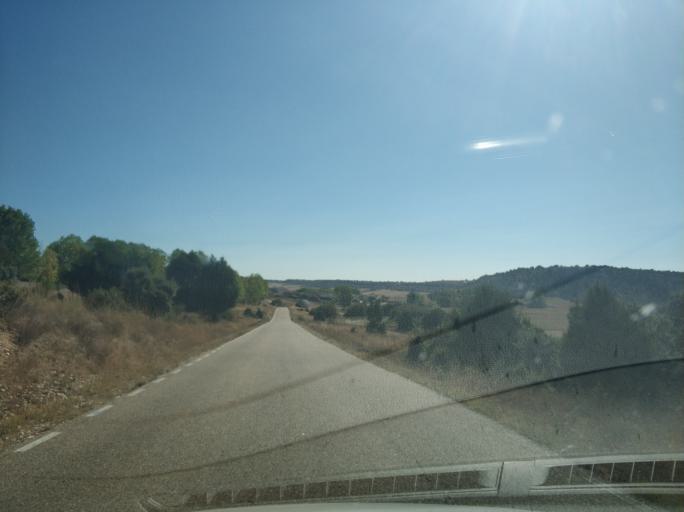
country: ES
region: Castille and Leon
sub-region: Provincia de Soria
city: Santa Maria de las Hoyas
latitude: 41.7746
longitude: -3.1768
